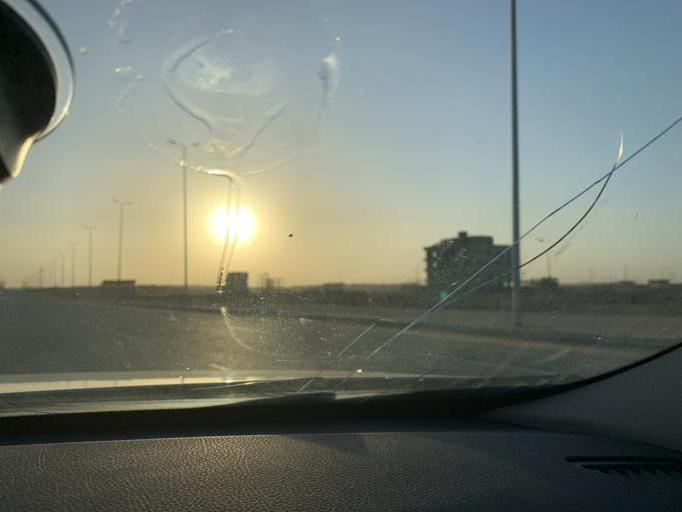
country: EG
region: Muhafazat al Qalyubiyah
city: Al Khankah
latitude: 30.0269
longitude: 31.5672
